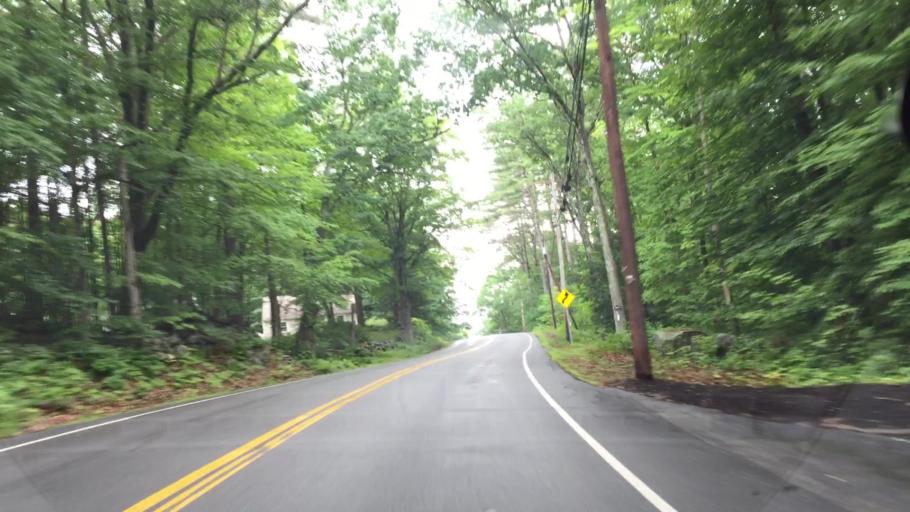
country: US
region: New Hampshire
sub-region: Carroll County
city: Center Harbor
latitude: 43.7352
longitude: -71.4770
